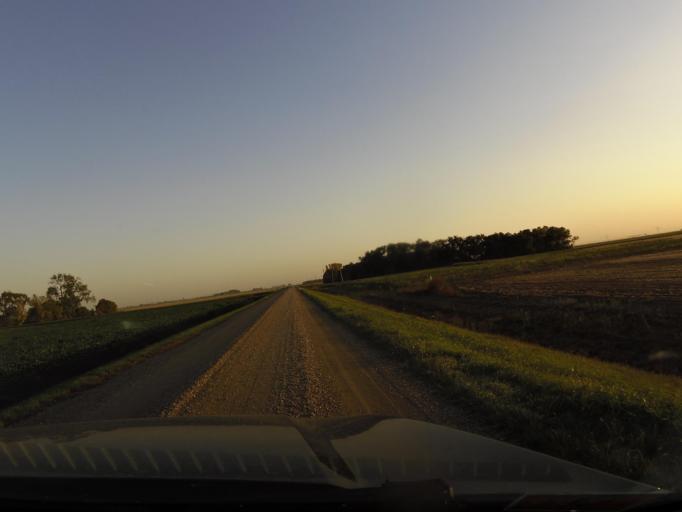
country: US
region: North Dakota
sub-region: Walsh County
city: Grafton
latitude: 48.3846
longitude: -97.2556
